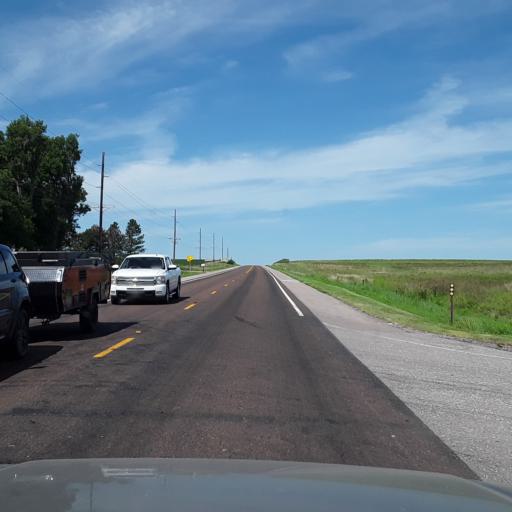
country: US
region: Nebraska
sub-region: Seward County
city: Milford
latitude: 40.8866
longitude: -96.8724
